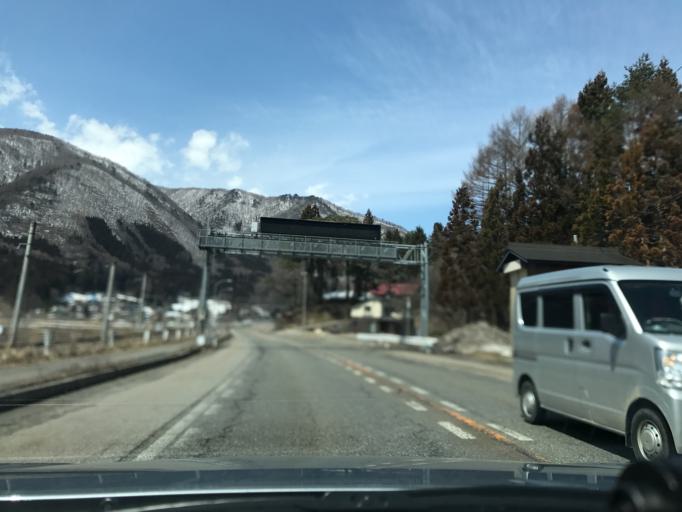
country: JP
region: Nagano
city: Omachi
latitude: 36.5676
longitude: 137.8406
